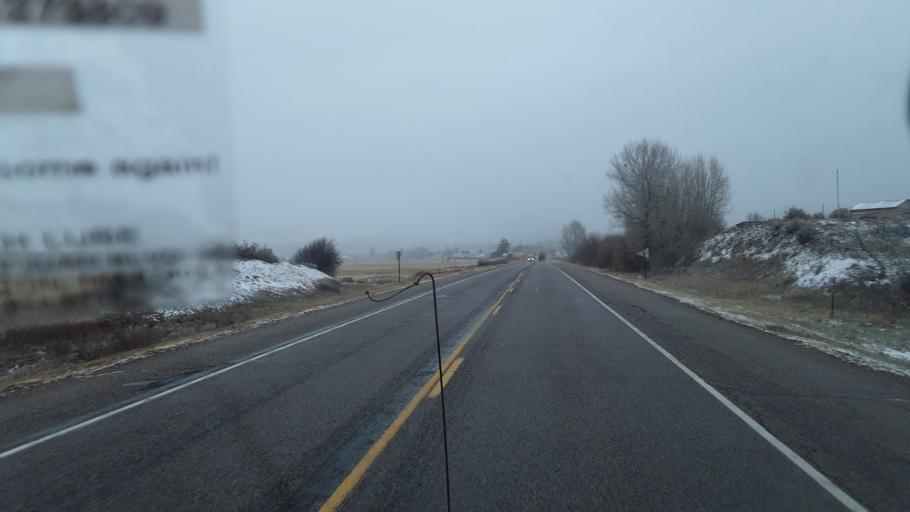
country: US
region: New Mexico
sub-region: Rio Arriba County
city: Tierra Amarilla
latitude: 36.7503
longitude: -106.5648
